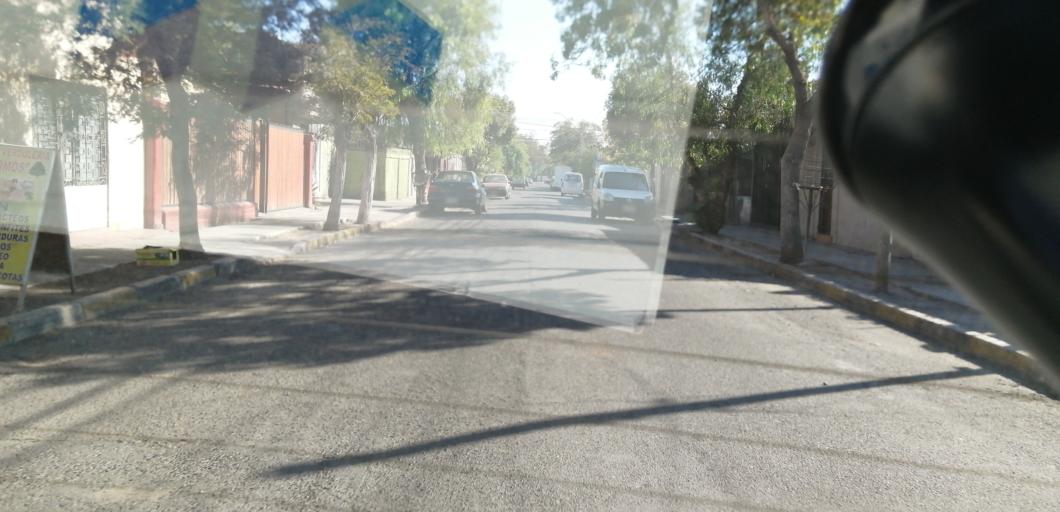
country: CL
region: Santiago Metropolitan
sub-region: Provincia de Santiago
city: Lo Prado
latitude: -33.4388
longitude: -70.7627
